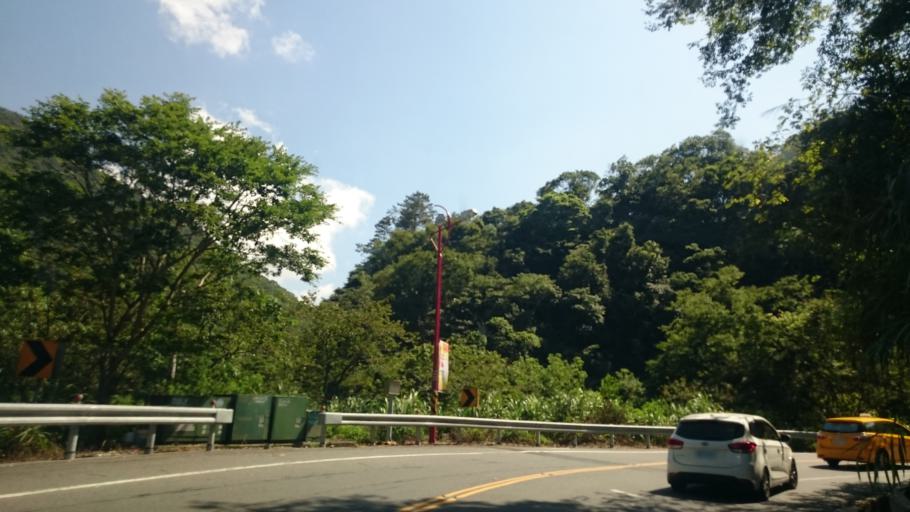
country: TW
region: Taiwan
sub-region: Nantou
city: Puli
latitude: 24.0144
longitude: 121.1201
